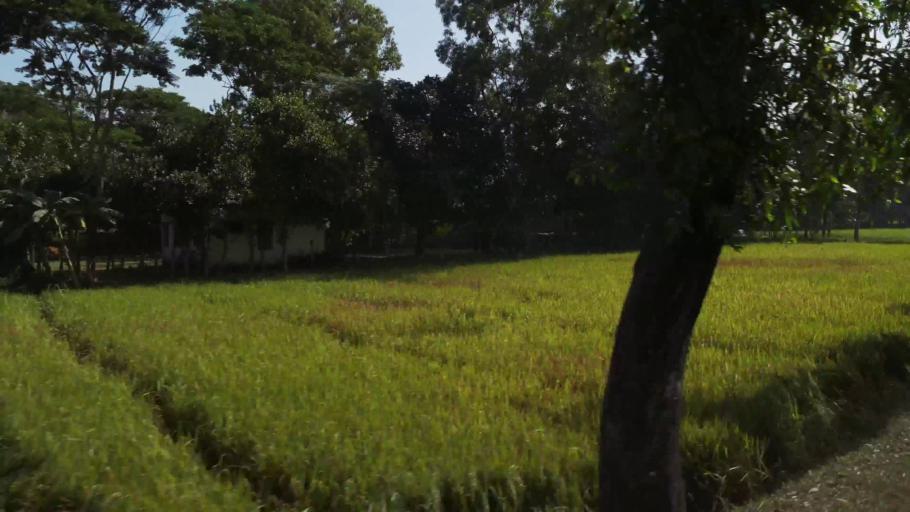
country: BD
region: Dhaka
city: Gafargaon
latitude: 24.5278
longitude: 90.5086
